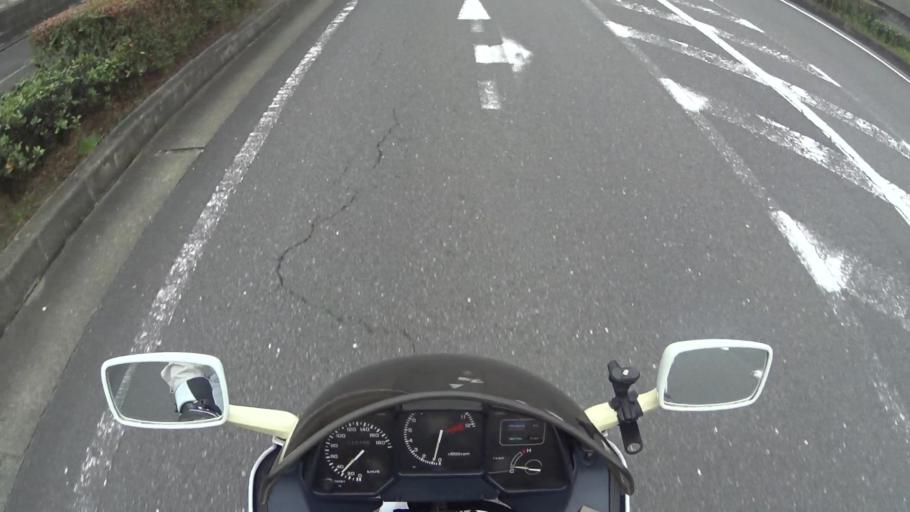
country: JP
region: Nara
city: Nara-shi
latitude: 34.7262
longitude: 135.7742
